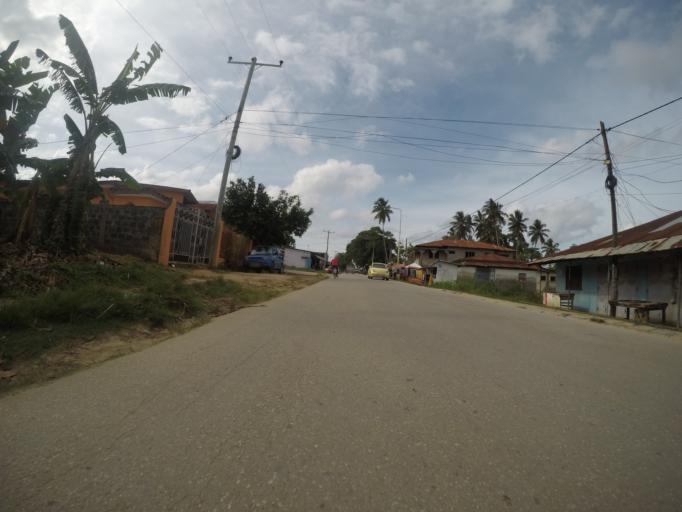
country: TZ
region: Pemba South
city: Chake Chake
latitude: -5.2384
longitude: 39.7802
